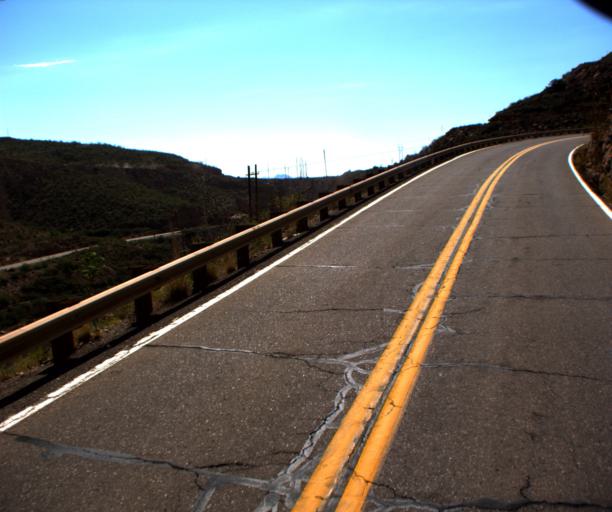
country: US
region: Arizona
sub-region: Greenlee County
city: Morenci
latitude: 33.0730
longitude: -109.3590
